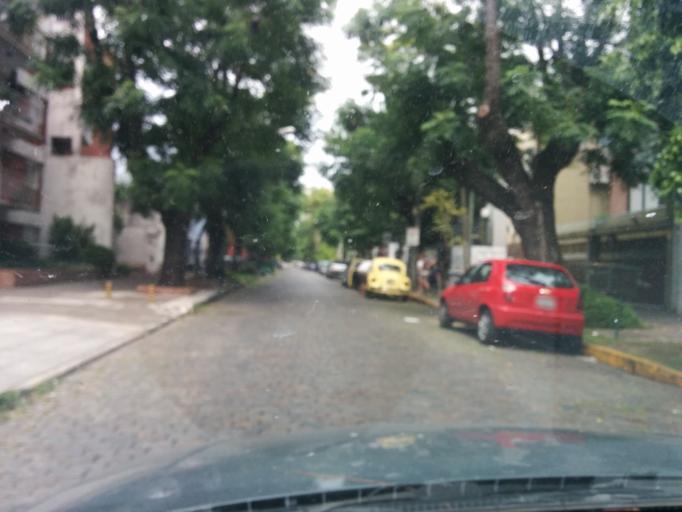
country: AR
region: Buenos Aires
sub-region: Partido de San Isidro
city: San Isidro
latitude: -34.4705
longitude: -58.5187
